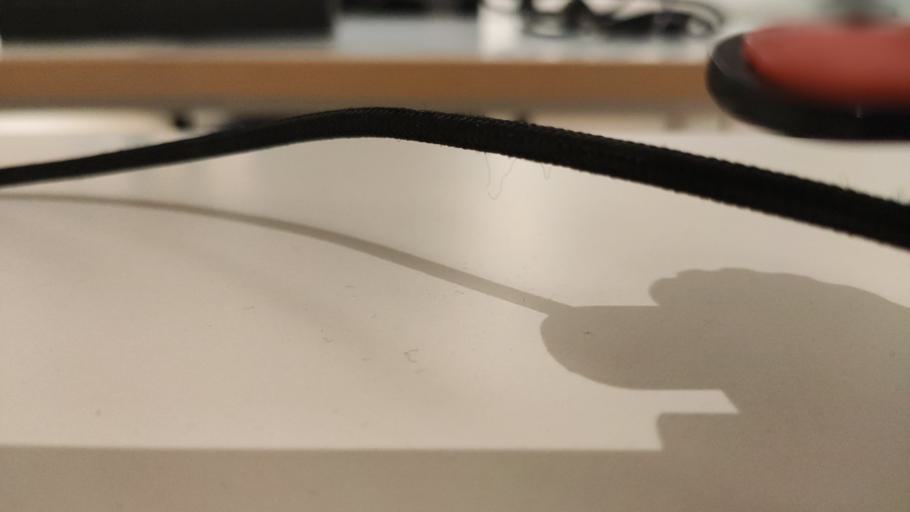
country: RU
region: Kaluga
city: Belousovo
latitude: 55.1420
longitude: 36.7729
